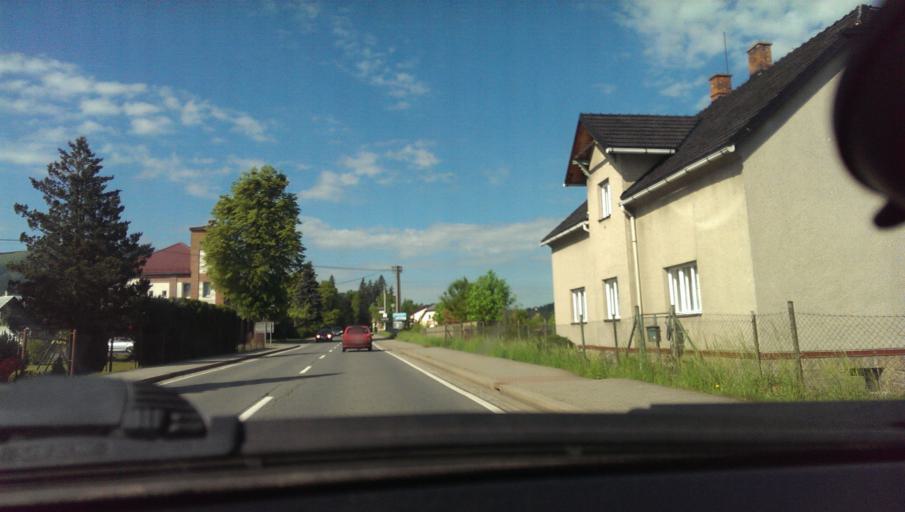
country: CZ
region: Moravskoslezsky
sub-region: Okres Frydek-Mistek
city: Celadna
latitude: 49.5463
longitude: 18.3353
